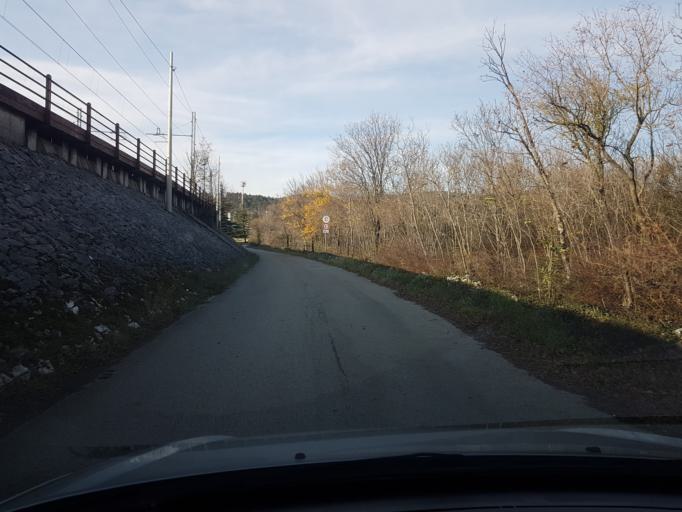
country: IT
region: Friuli Venezia Giulia
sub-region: Provincia di Trieste
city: Sistiana-Visogliano
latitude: 45.7774
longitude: 13.6422
